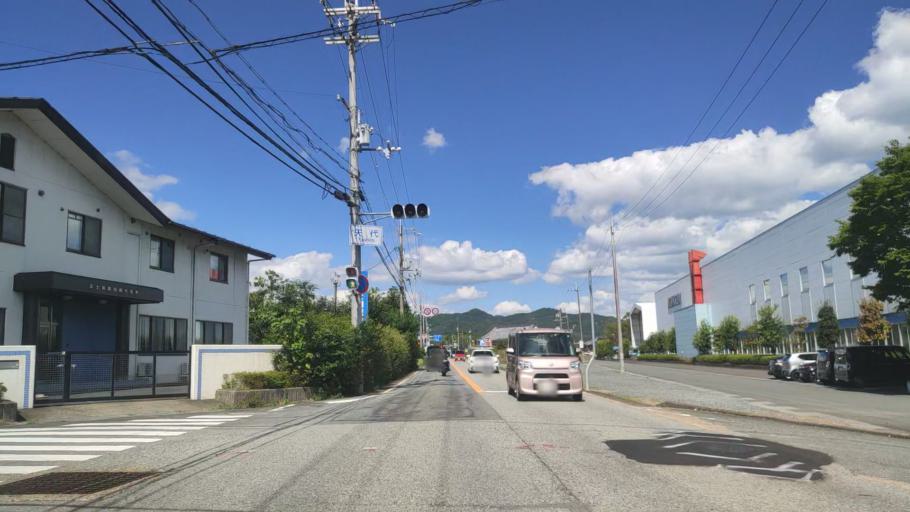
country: JP
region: Kyoto
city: Fukuchiyama
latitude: 35.2243
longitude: 135.1300
